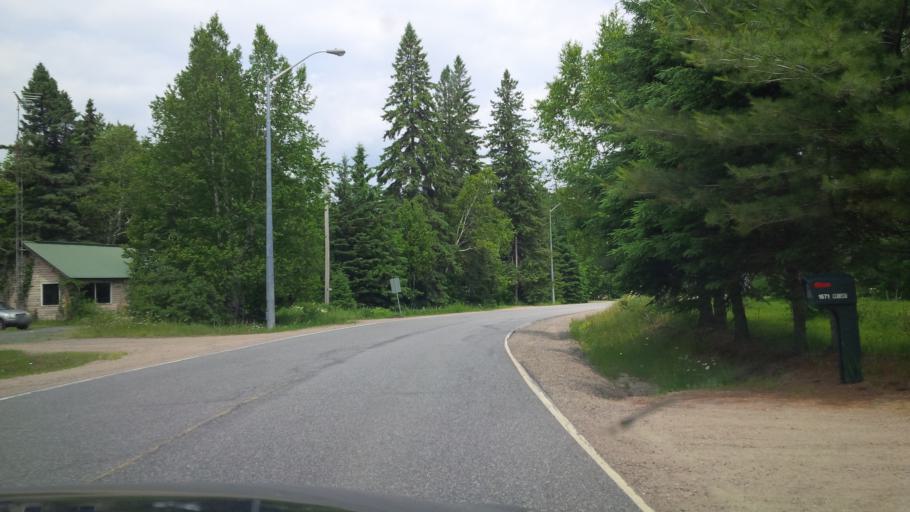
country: CA
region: Ontario
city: Huntsville
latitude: 45.5550
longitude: -79.2309
